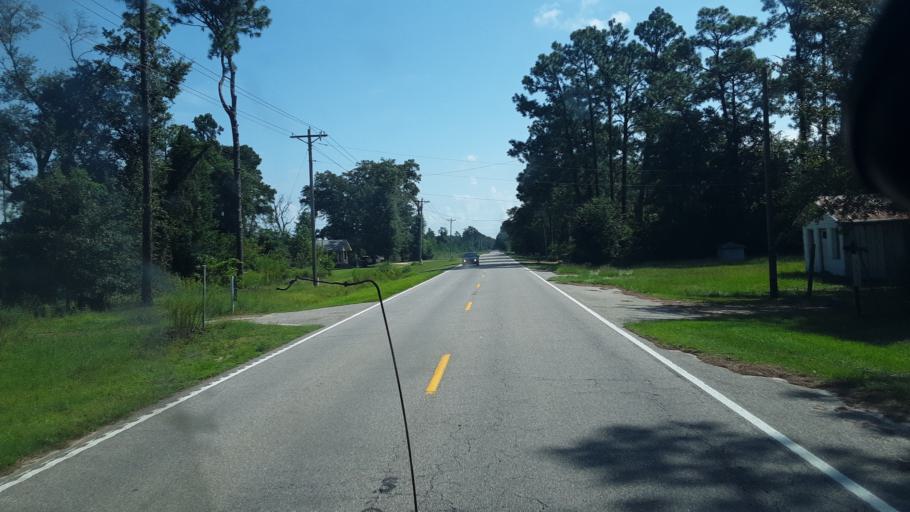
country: US
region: South Carolina
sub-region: Hampton County
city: Varnville
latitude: 32.8789
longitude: -81.0363
